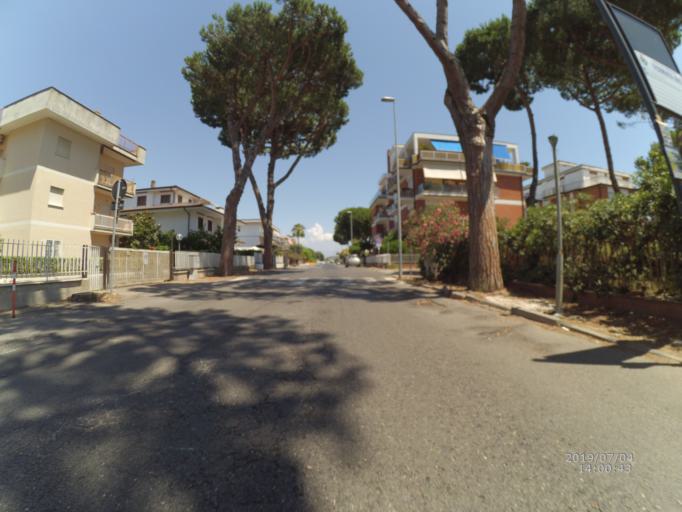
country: IT
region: Latium
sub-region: Provincia di Latina
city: Terracina
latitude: 41.2860
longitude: 13.2199
